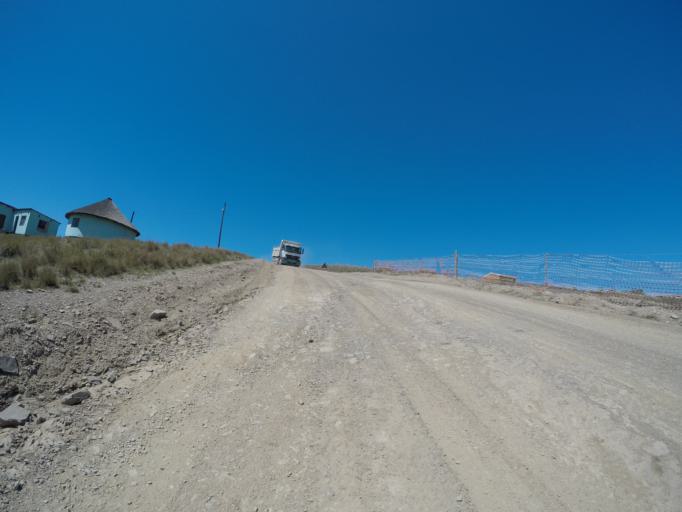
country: ZA
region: Eastern Cape
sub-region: OR Tambo District Municipality
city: Libode
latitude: -32.0194
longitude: 29.1152
